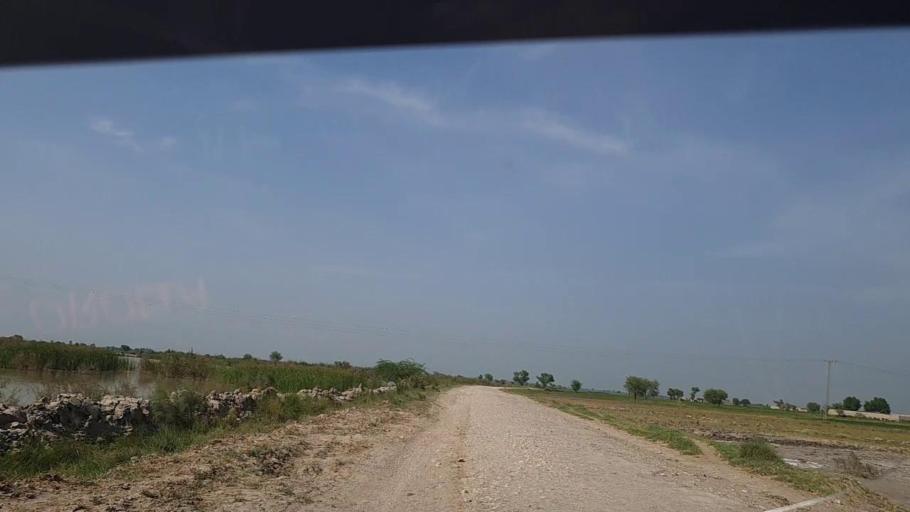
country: PK
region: Sindh
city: Khanpur
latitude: 27.8437
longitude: 69.3758
